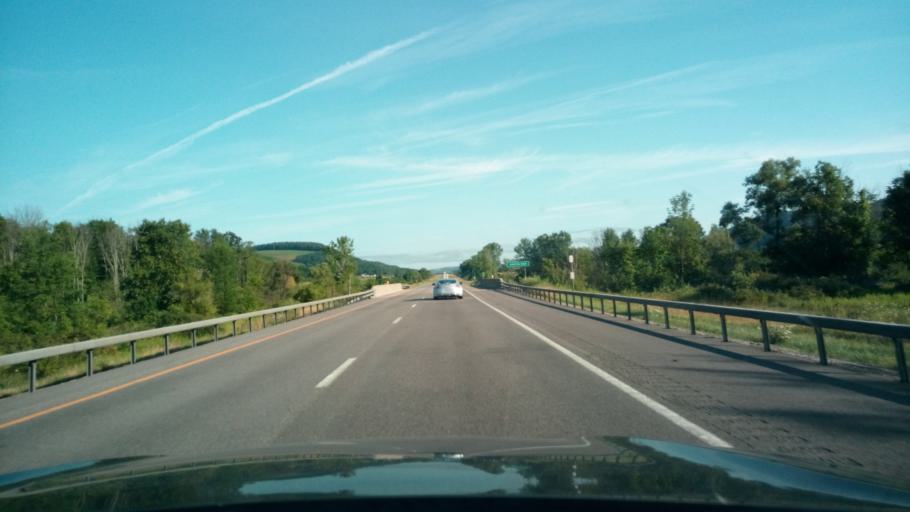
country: US
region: New York
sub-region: Steuben County
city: Wayland
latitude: 42.4488
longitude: -77.4737
